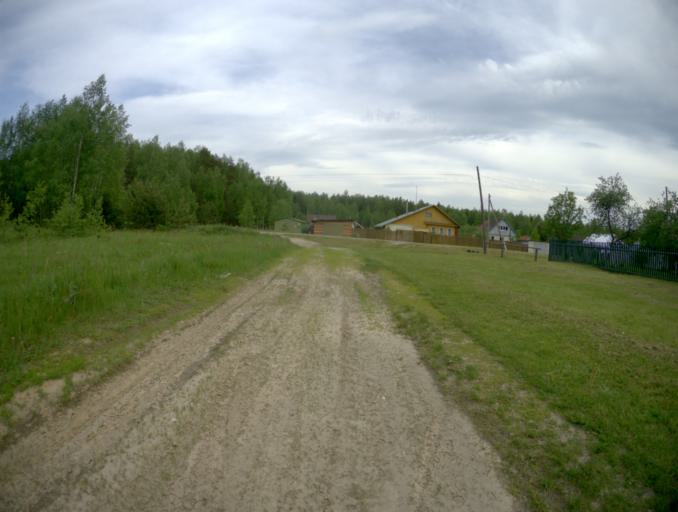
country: RU
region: Vladimir
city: Ivanishchi
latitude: 55.8332
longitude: 40.5084
